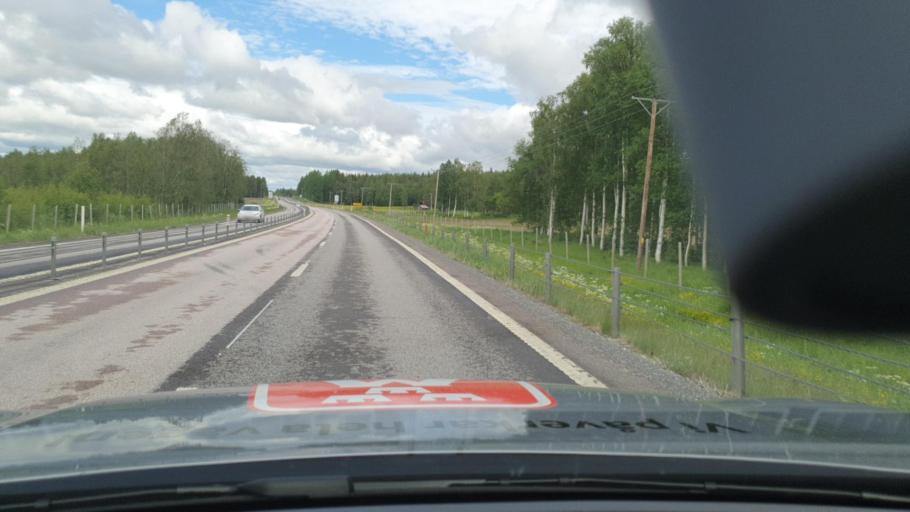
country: SE
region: Norrbotten
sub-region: Lulea Kommun
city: Ranea
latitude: 65.7522
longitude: 22.1713
